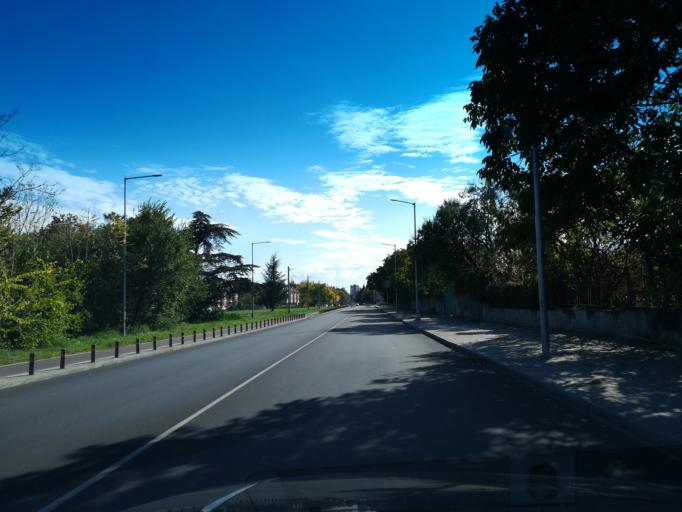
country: BG
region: Stara Zagora
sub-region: Obshtina Stara Zagora
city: Stara Zagora
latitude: 42.4409
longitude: 25.6351
